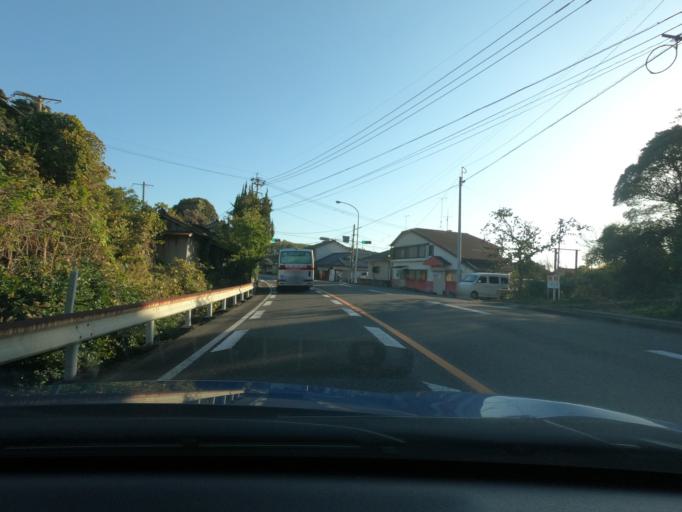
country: JP
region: Kagoshima
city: Akune
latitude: 31.9923
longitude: 130.1974
